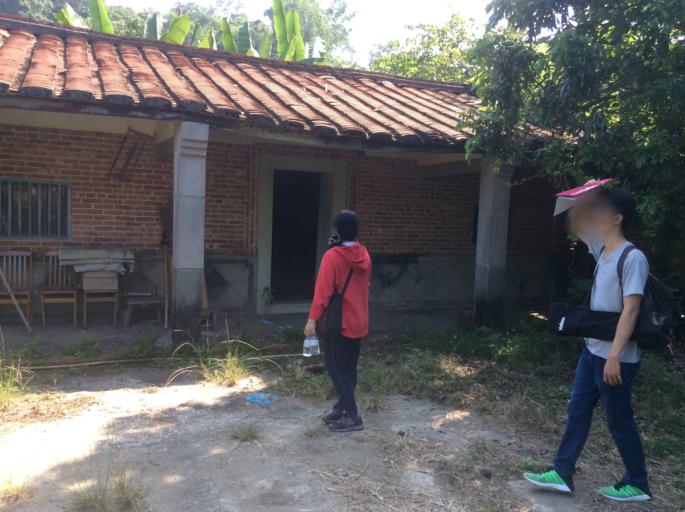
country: TW
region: Taiwan
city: Yujing
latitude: 22.9956
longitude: 120.4372
